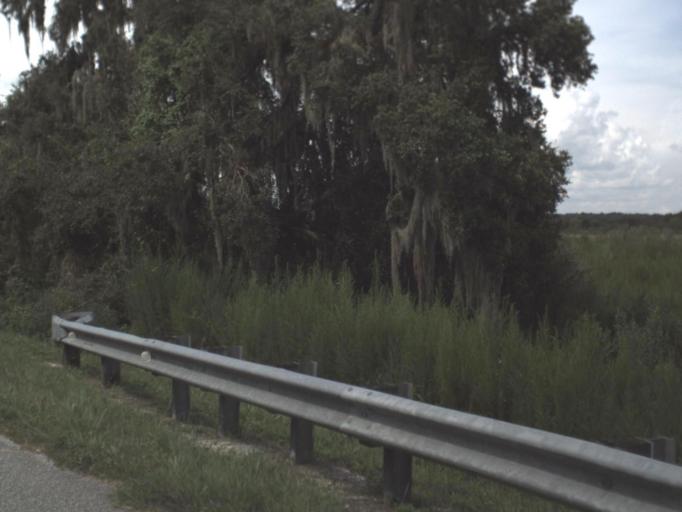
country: US
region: Florida
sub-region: Hernando County
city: Brooksville
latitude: 28.5767
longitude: -82.3753
